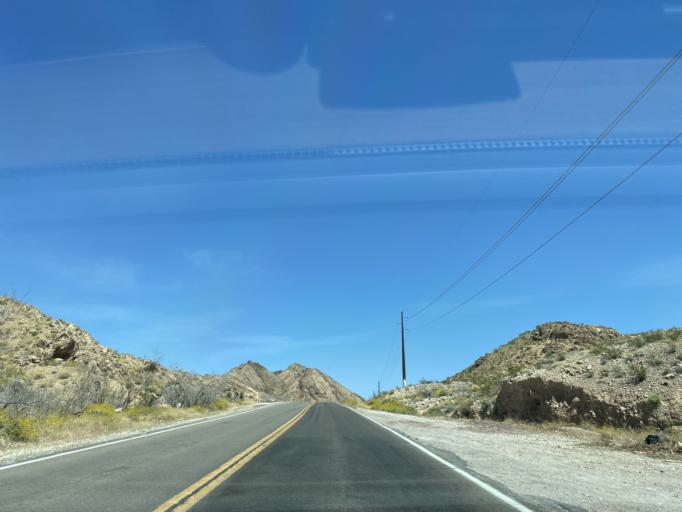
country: US
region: Nevada
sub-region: Clark County
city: Nellis Air Force Base
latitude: 36.2003
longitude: -114.9959
